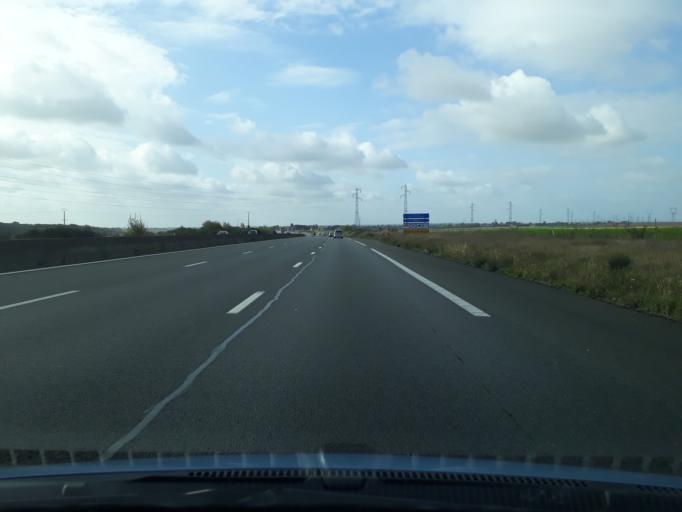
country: FR
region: Centre
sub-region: Departement du Loir-et-Cher
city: Montlivault
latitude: 47.6749
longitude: 1.3989
